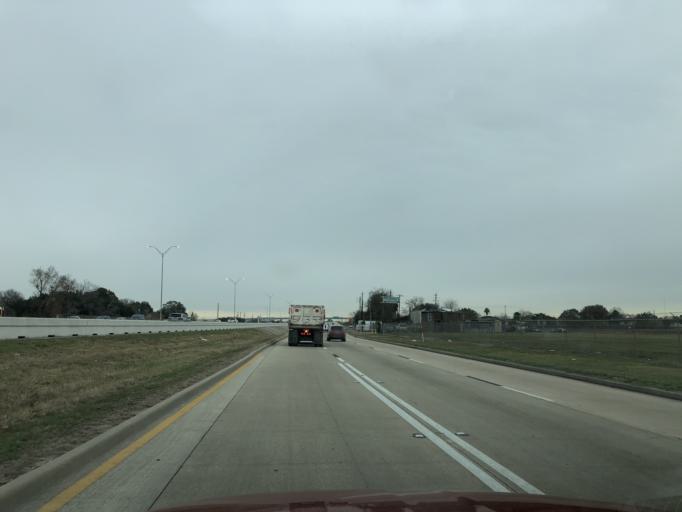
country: US
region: Texas
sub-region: Fort Bend County
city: Missouri City
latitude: 29.6179
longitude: -95.5027
